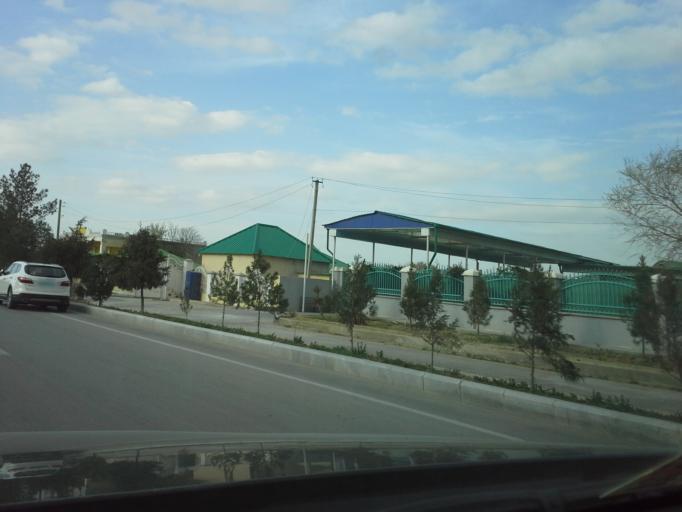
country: TM
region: Ahal
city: Abadan
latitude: 37.9599
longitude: 58.2241
